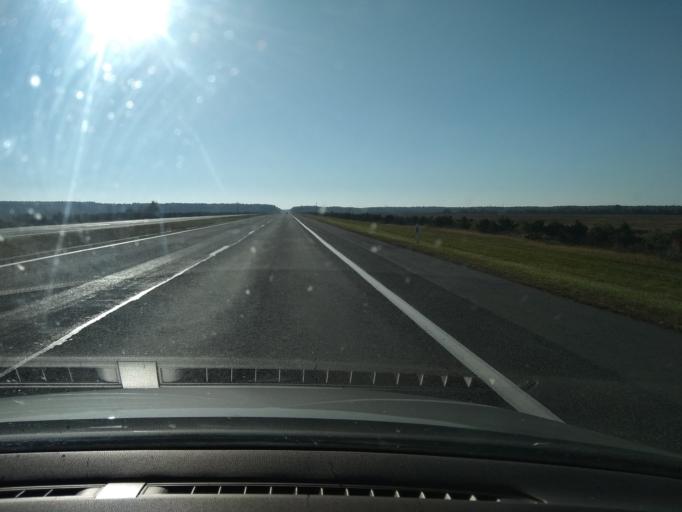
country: BY
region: Brest
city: Ivatsevichy
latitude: 52.6679
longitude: 25.2980
